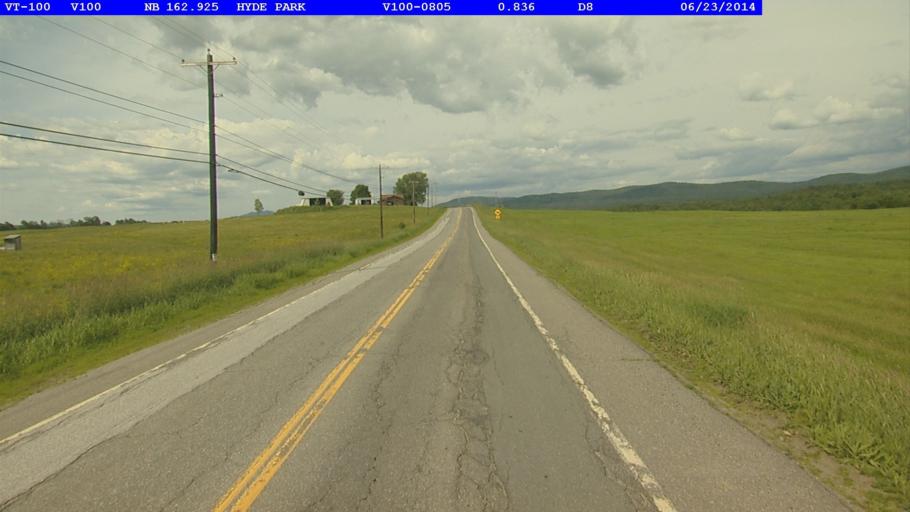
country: US
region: Vermont
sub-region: Lamoille County
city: Hyde Park
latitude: 44.6087
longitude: -72.6106
